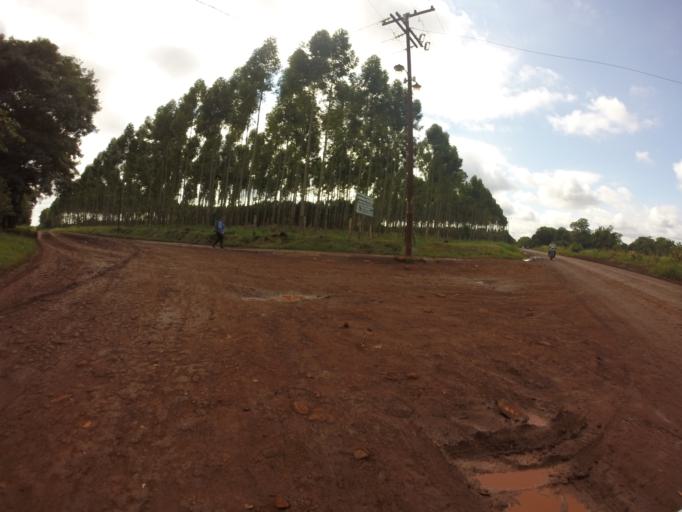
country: PY
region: Alto Parana
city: Ciudad del Este
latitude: -25.4111
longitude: -54.6616
